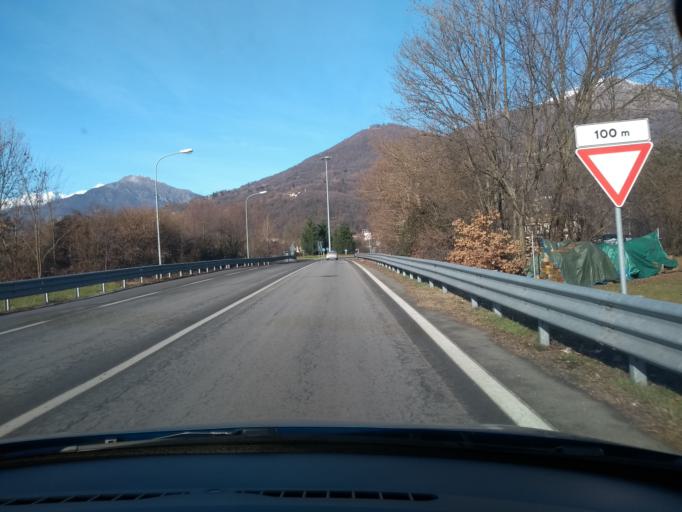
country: IT
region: Piedmont
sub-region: Provincia di Torino
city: Cuorgne
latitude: 45.4005
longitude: 7.6587
